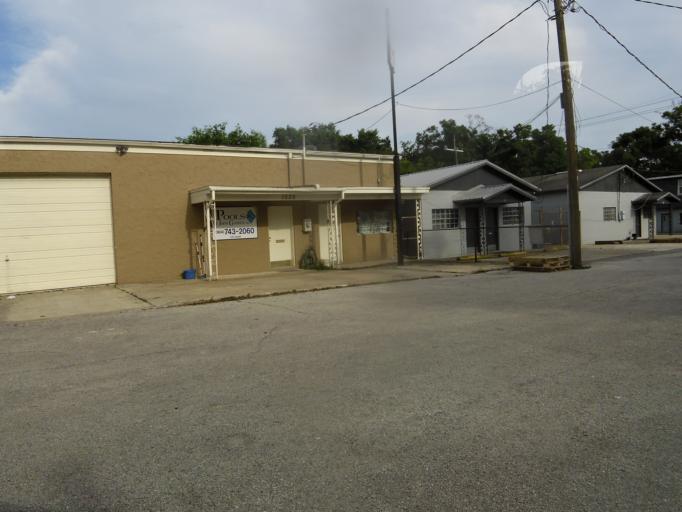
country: US
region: Florida
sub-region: Duval County
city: Jacksonville
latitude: 30.3364
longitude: -81.6018
